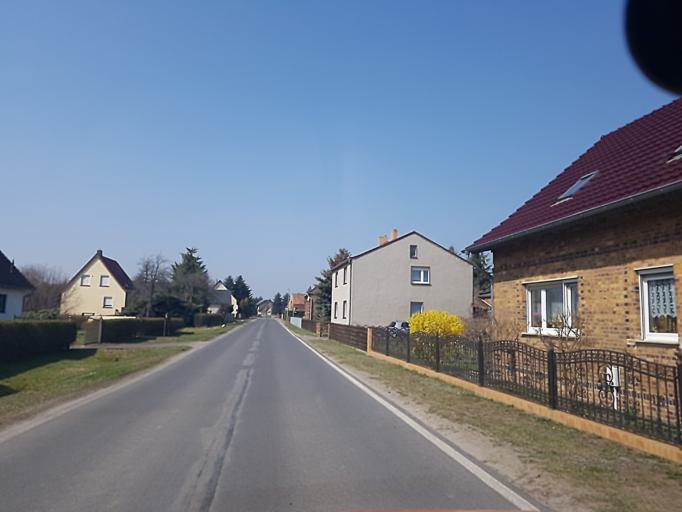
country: DE
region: Brandenburg
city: Forst
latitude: 51.6807
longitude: 14.5655
